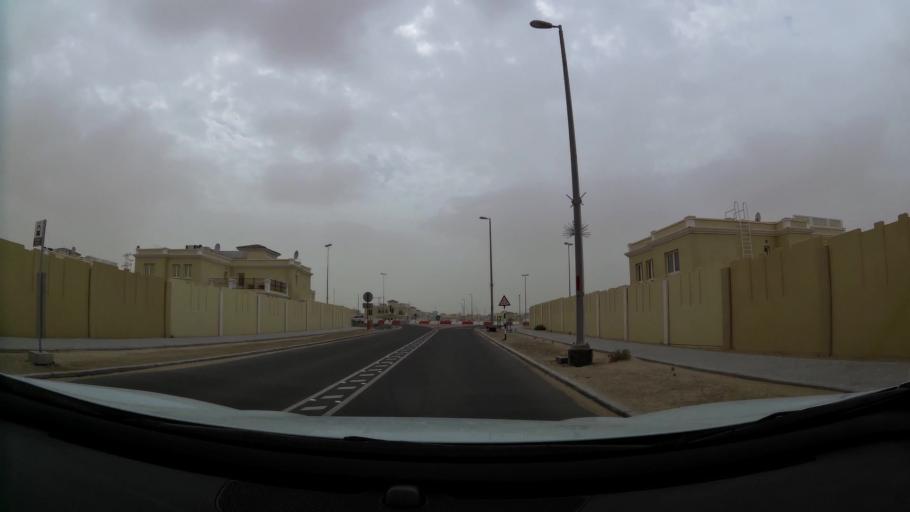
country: AE
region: Abu Dhabi
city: Abu Dhabi
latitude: 24.4514
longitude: 54.7429
